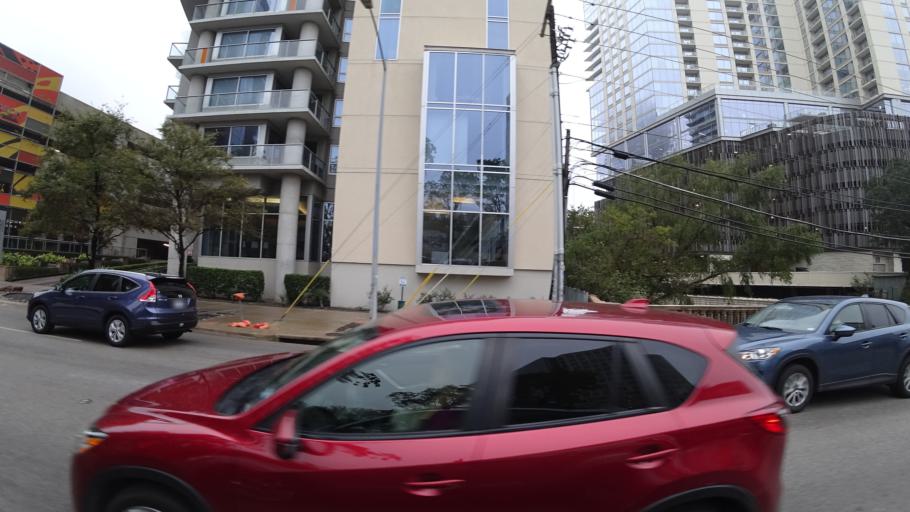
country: US
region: Texas
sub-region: Travis County
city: Austin
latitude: 30.2696
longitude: -97.7523
